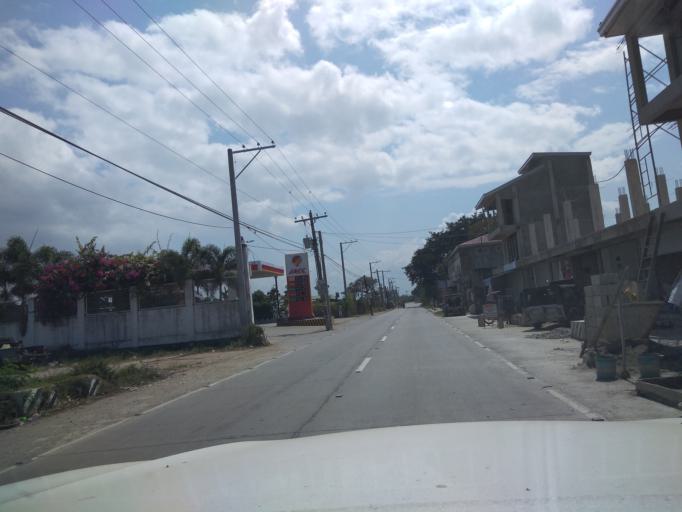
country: PH
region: Central Luzon
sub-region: Province of Pampanga
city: Talang
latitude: 15.0243
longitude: 120.8423
